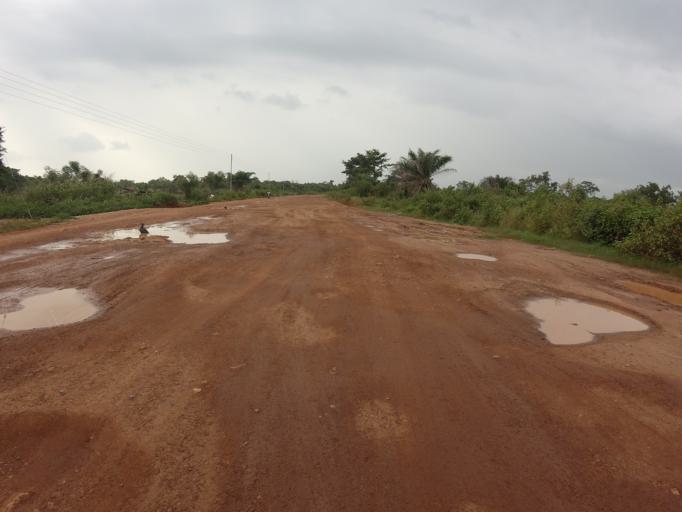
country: GH
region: Volta
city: Kpandu
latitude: 7.0084
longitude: 0.4295
